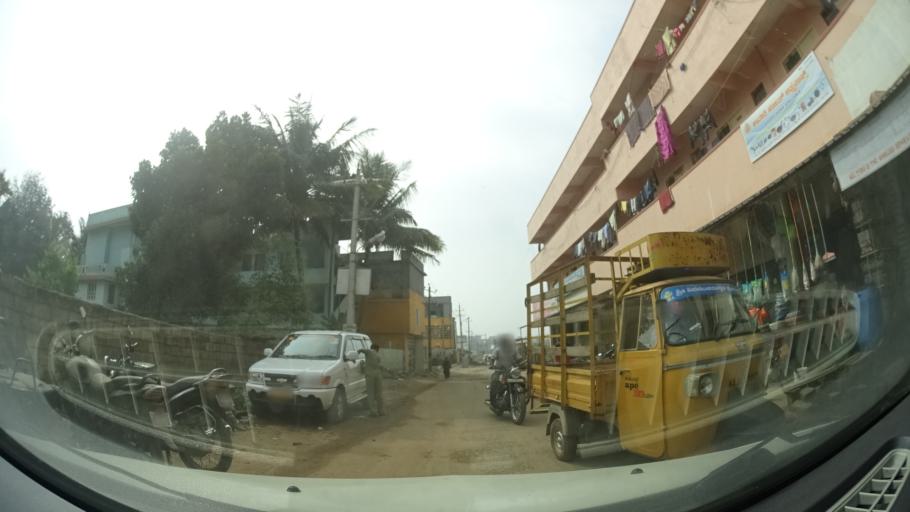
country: IN
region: Karnataka
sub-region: Bangalore Urban
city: Anekal
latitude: 12.8289
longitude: 77.6689
